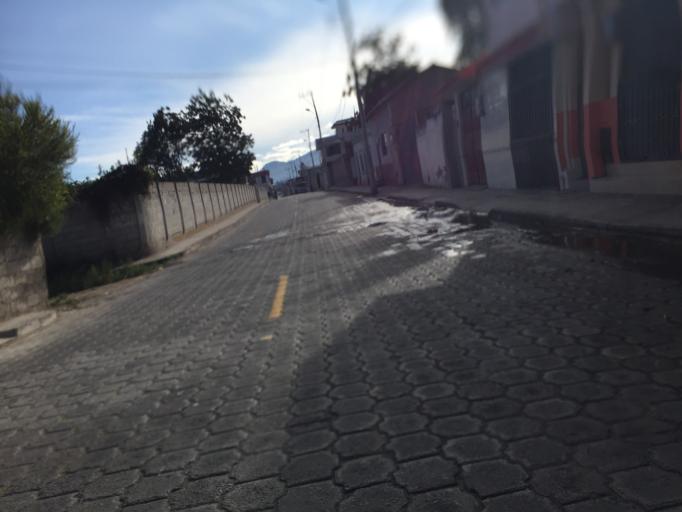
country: EC
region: Imbabura
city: Atuntaqui
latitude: 0.3378
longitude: -78.1959
